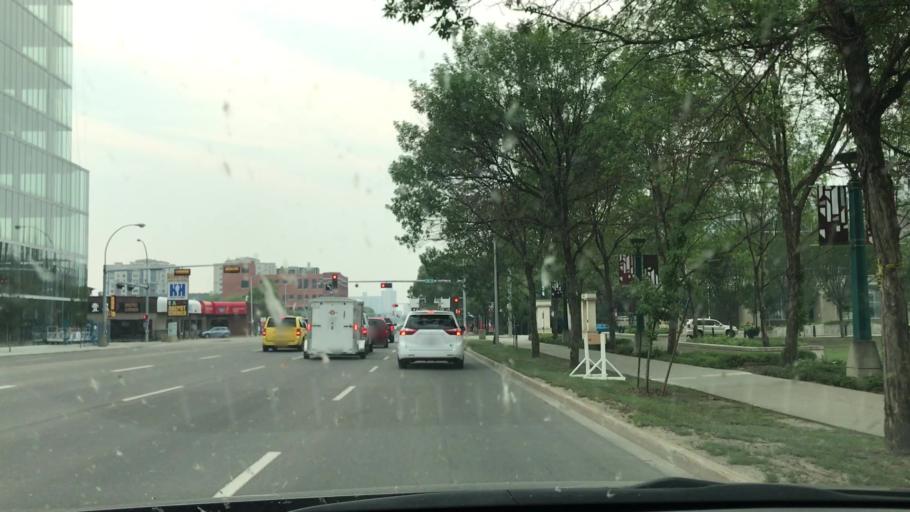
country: CA
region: Alberta
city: Edmonton
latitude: 53.5463
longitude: -113.5034
